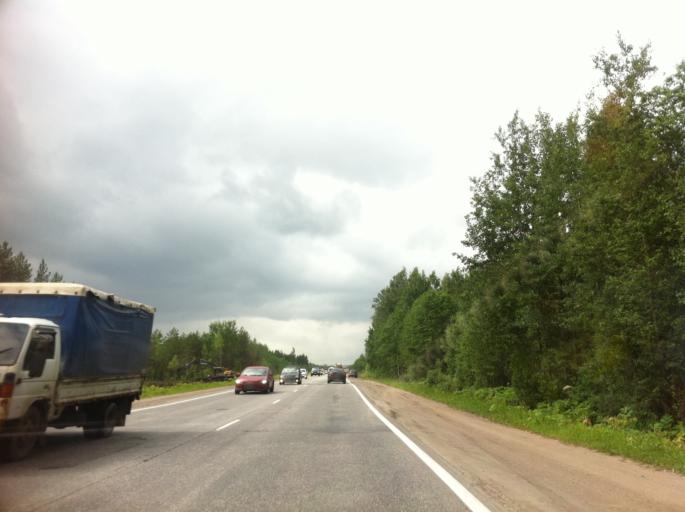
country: RU
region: Leningrad
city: Gatchina
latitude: 59.5265
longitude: 30.1057
